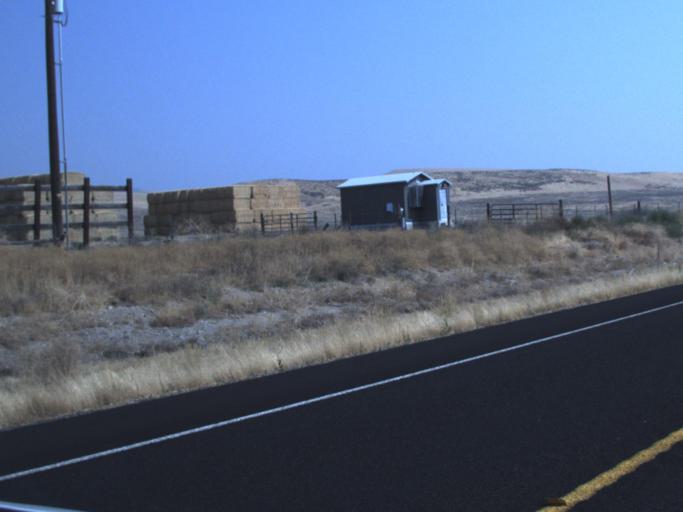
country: US
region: Washington
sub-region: Yakima County
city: Zillah
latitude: 46.5058
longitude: -120.1662
